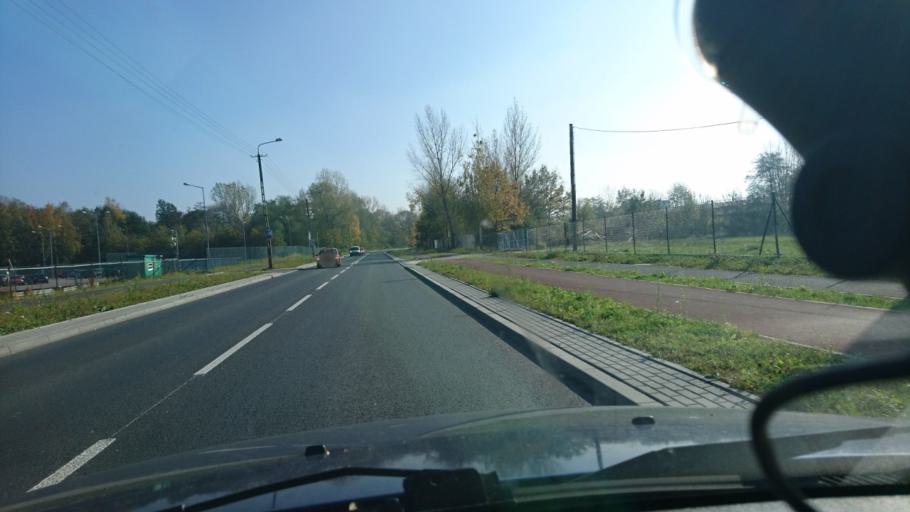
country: PL
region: Silesian Voivodeship
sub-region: Powiat bielski
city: Mazancowice
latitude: 49.8257
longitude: 18.9721
